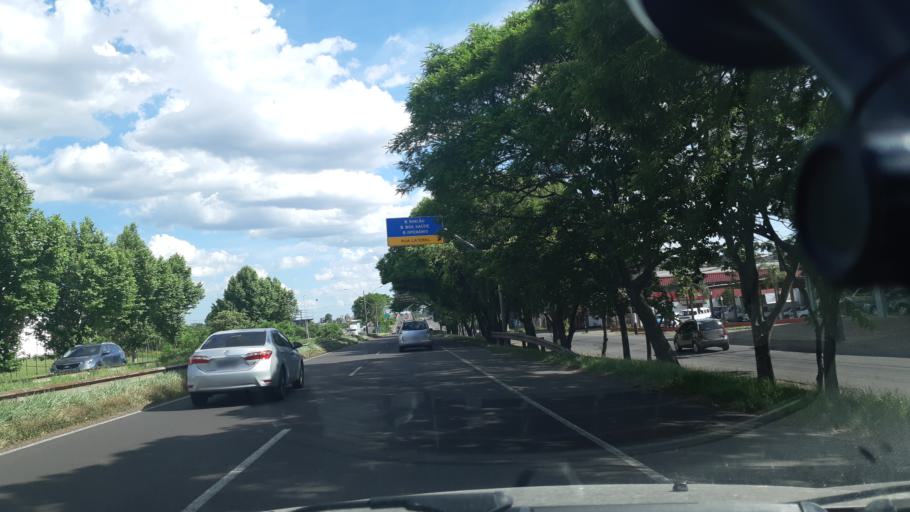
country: BR
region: Rio Grande do Sul
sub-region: Novo Hamburgo
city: Novo Hamburgo
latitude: -29.6640
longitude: -51.1437
